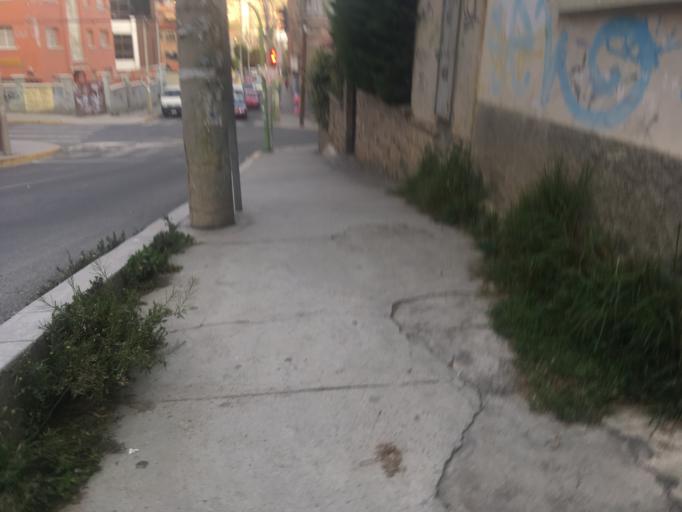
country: BO
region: La Paz
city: La Paz
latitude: -16.5037
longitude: -68.1233
